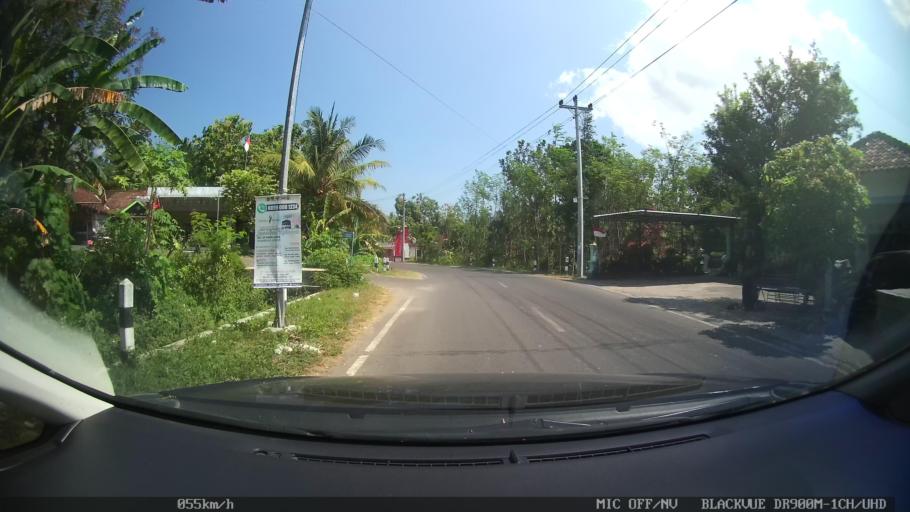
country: ID
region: Daerah Istimewa Yogyakarta
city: Pundong
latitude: -7.9628
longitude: 110.3562
